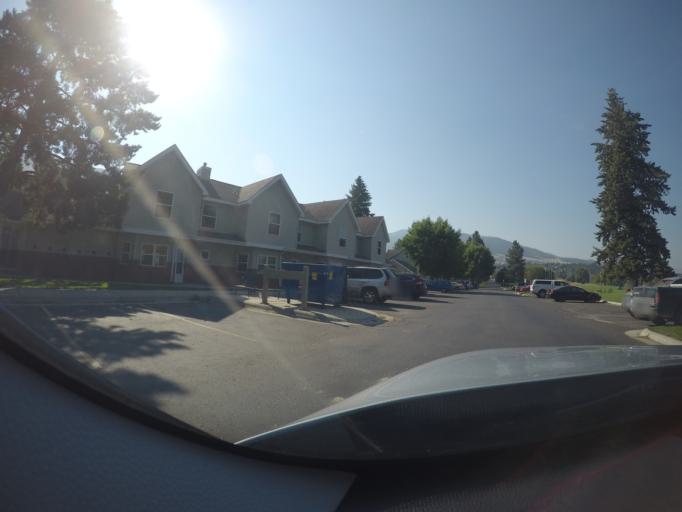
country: US
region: Montana
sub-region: Missoula County
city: Missoula
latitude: 46.8485
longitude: -113.9933
